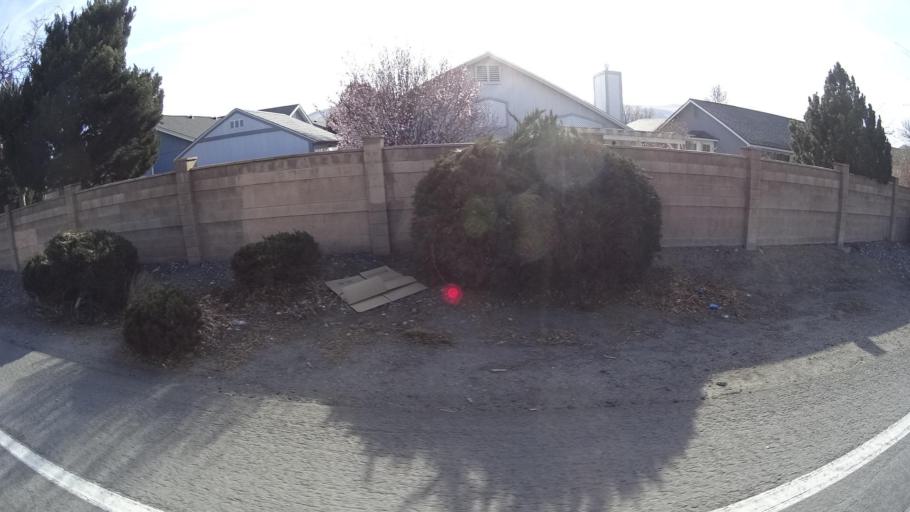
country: US
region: Nevada
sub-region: Washoe County
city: Sparks
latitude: 39.5445
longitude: -119.7148
